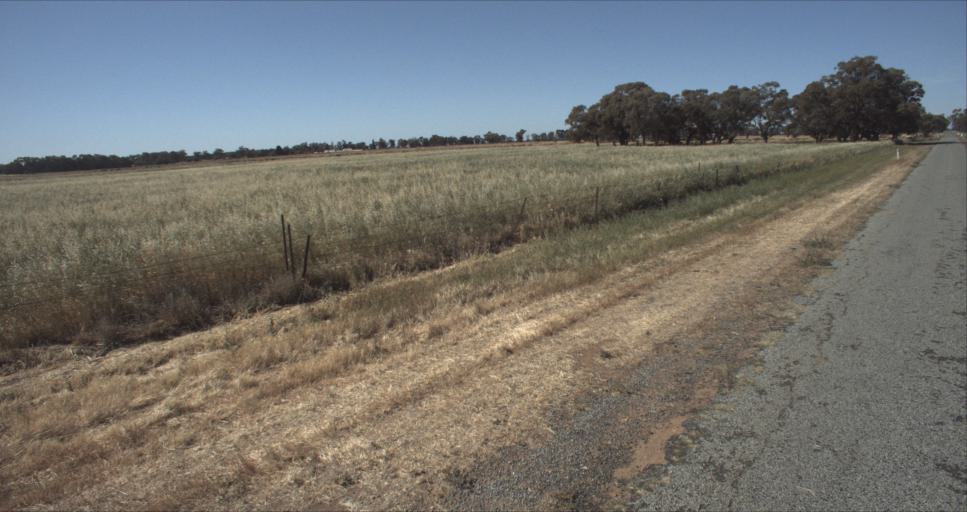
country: AU
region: New South Wales
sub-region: Leeton
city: Leeton
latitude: -34.5377
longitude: 146.3171
